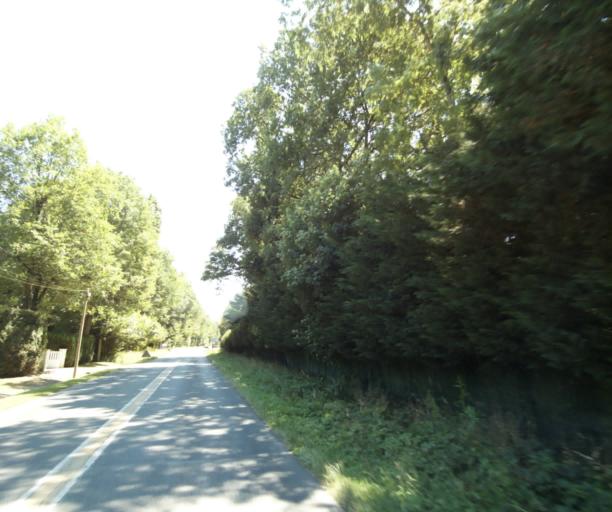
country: FR
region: Ile-de-France
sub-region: Departement de Seine-et-Marne
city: Noisy-sur-Ecole
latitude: 48.3859
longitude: 2.4953
